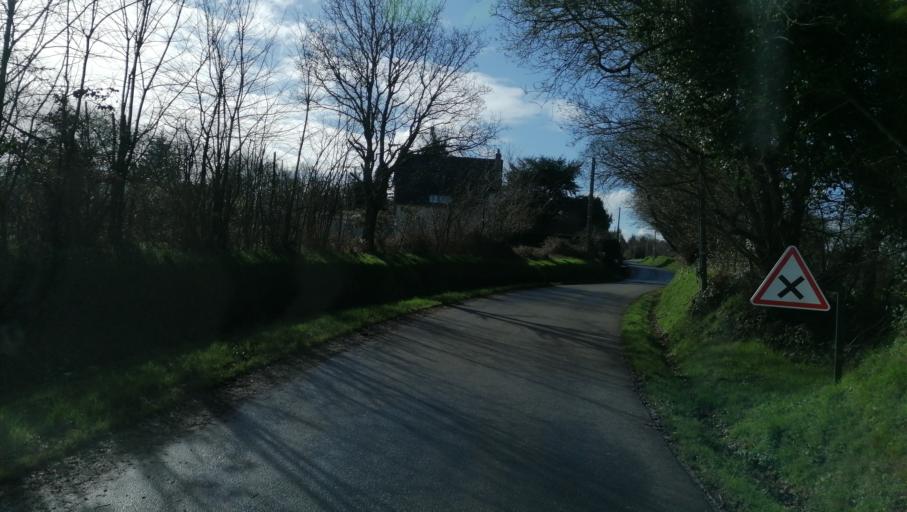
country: FR
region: Brittany
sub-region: Departement des Cotes-d'Armor
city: Plouha
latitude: 48.6630
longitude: -2.9330
